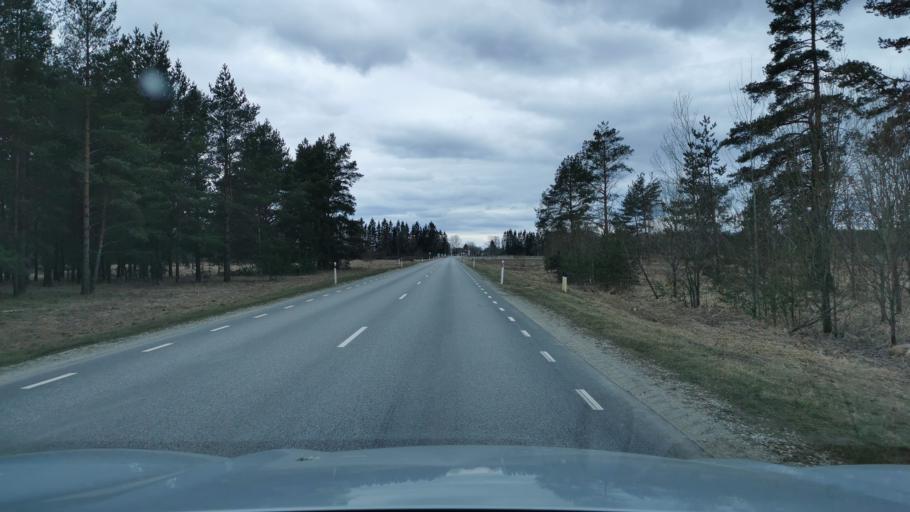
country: EE
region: Ida-Virumaa
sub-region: Puessi linn
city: Pussi
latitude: 59.3606
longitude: 27.0251
